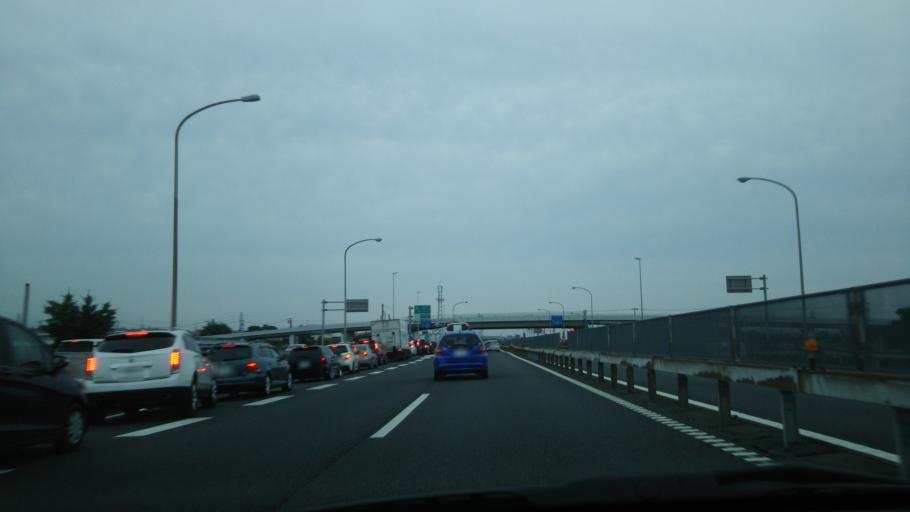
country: JP
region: Kanagawa
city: Isehara
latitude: 35.3842
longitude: 139.3306
